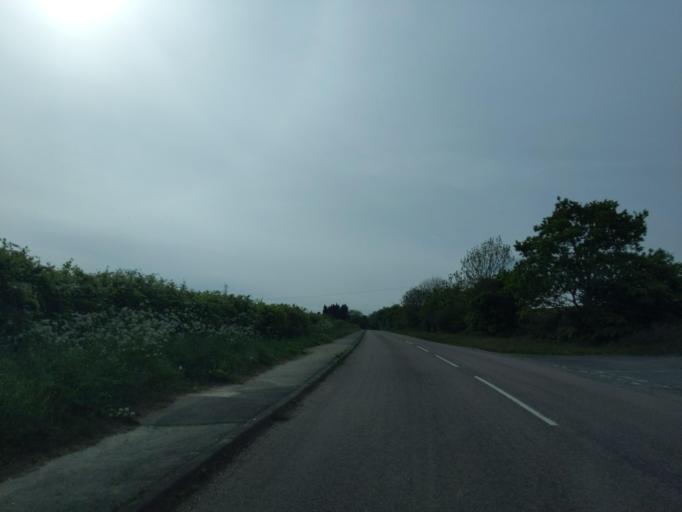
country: GB
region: England
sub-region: Devon
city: Yelverton
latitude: 50.4438
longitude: -4.0893
